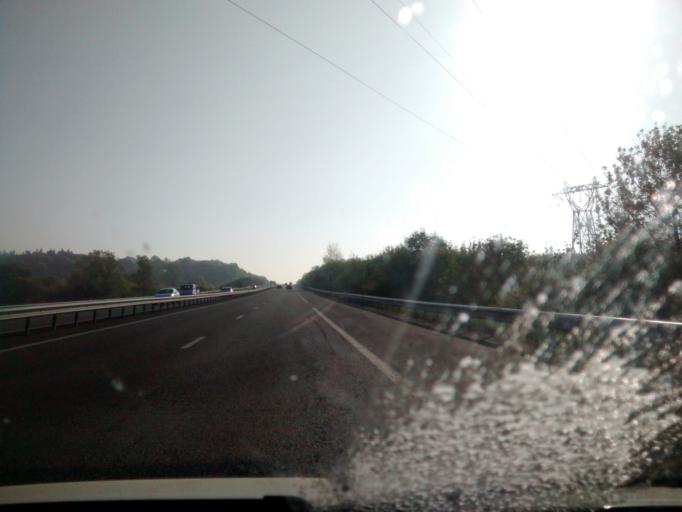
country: FR
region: Brittany
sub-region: Departement d'Ille-et-Vilaine
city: Gosne
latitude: 48.2396
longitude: -1.4653
